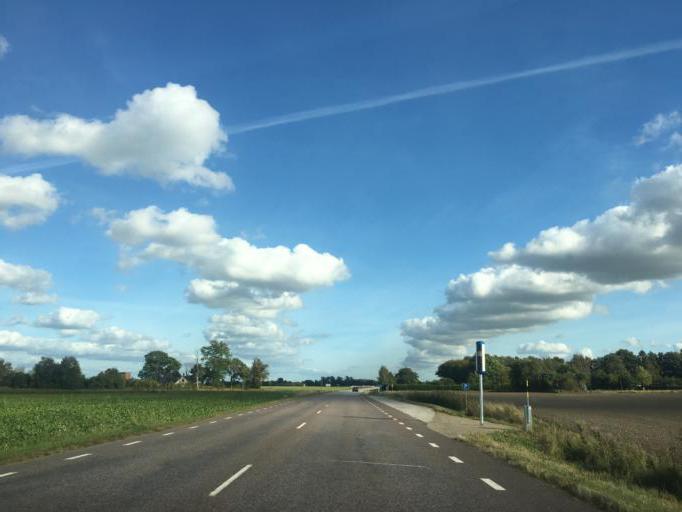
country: SE
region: Skane
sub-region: Lunds Kommun
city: Lund
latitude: 55.7955
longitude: 13.2011
